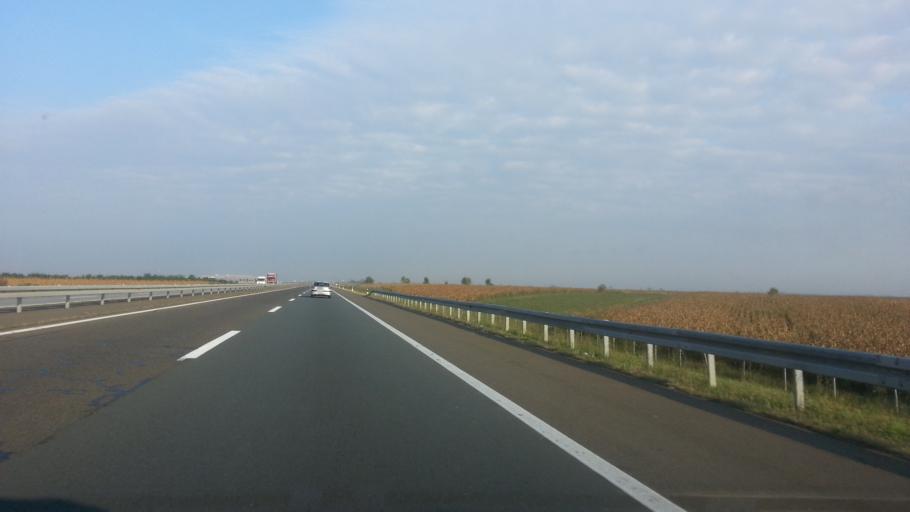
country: RS
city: Novi Banovci
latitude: 44.9550
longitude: 20.2608
